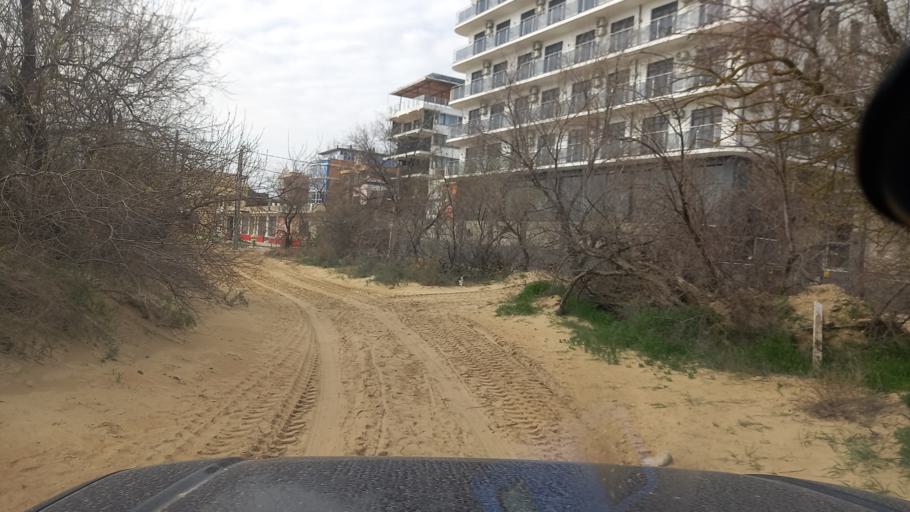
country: RU
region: Krasnodarskiy
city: Vityazevo
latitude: 44.9845
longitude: 37.2487
